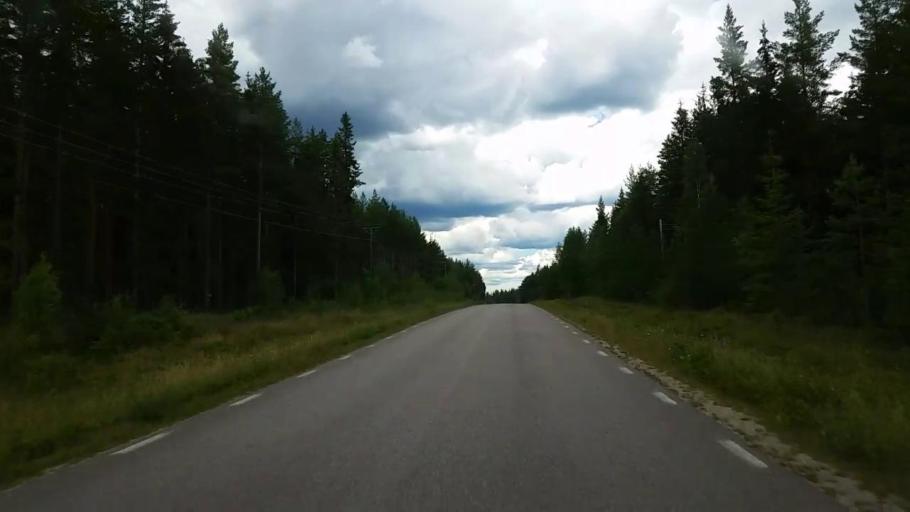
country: SE
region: Gaevleborg
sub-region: Ovanakers Kommun
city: Edsbyn
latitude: 61.4267
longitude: 15.8993
